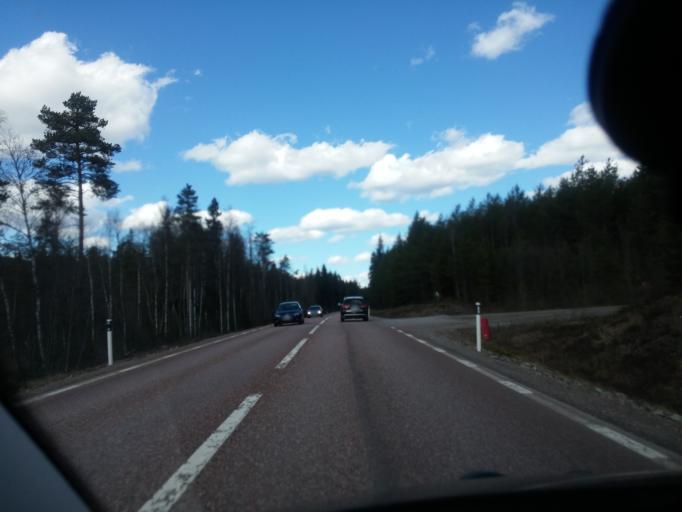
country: SE
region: Dalarna
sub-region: Faluns Kommun
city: Svardsjo
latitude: 60.7687
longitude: 15.7555
